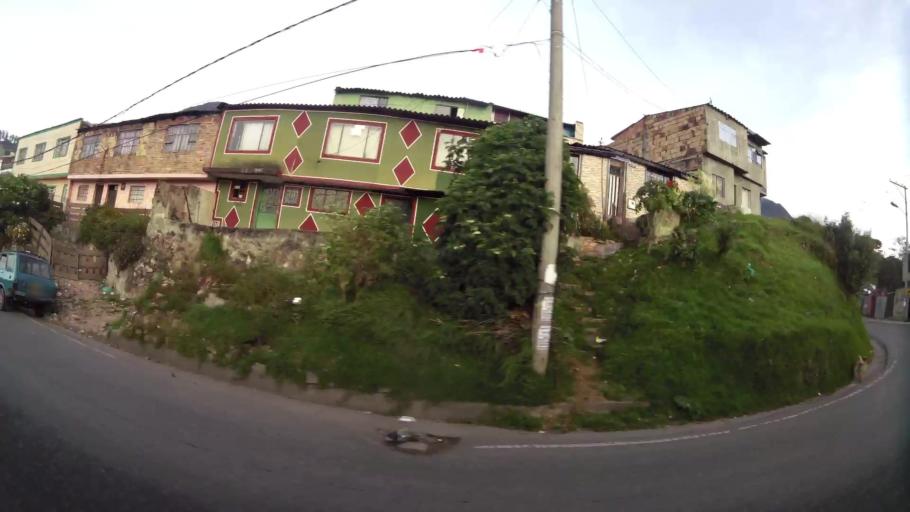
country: CO
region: Bogota D.C.
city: Bogota
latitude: 4.5401
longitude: -74.0836
